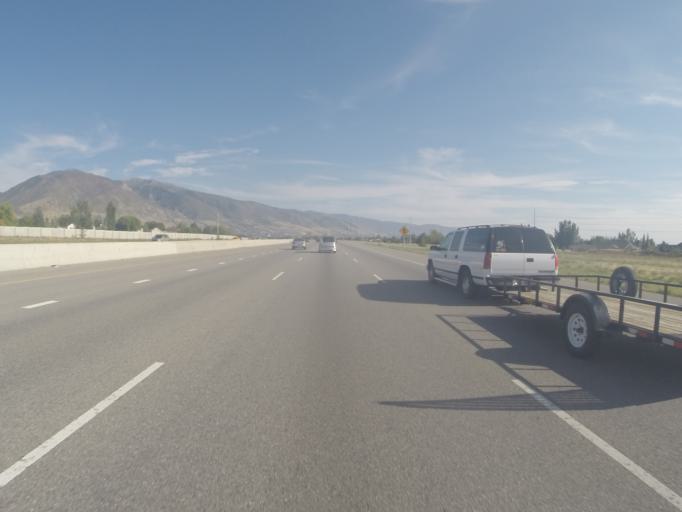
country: US
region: Utah
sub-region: Davis County
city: Kaysville
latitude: 41.0080
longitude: -111.9337
